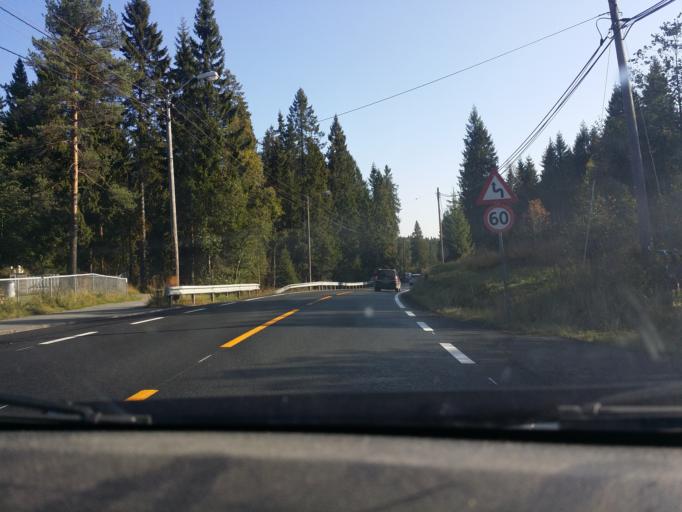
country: NO
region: Akershus
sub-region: Baerum
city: Skui
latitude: 59.9568
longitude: 10.3706
